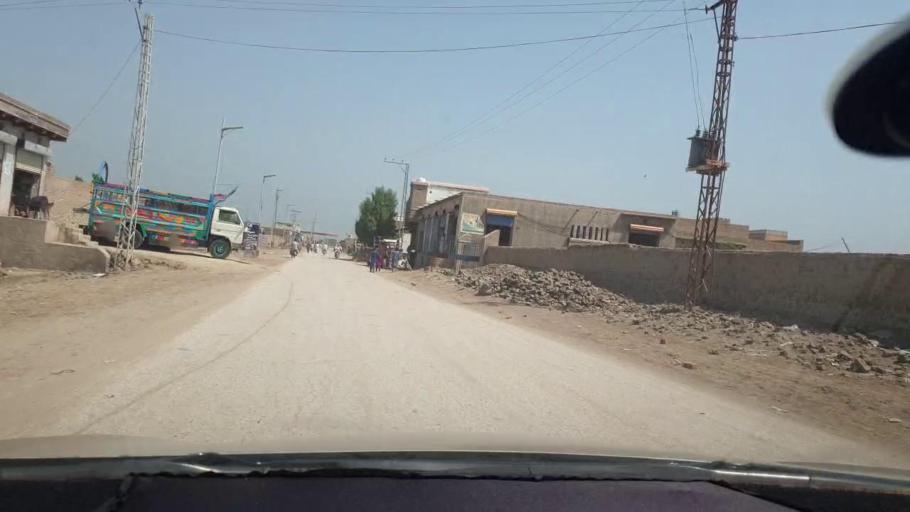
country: PK
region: Sindh
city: Kambar
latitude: 27.5892
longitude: 67.9921
